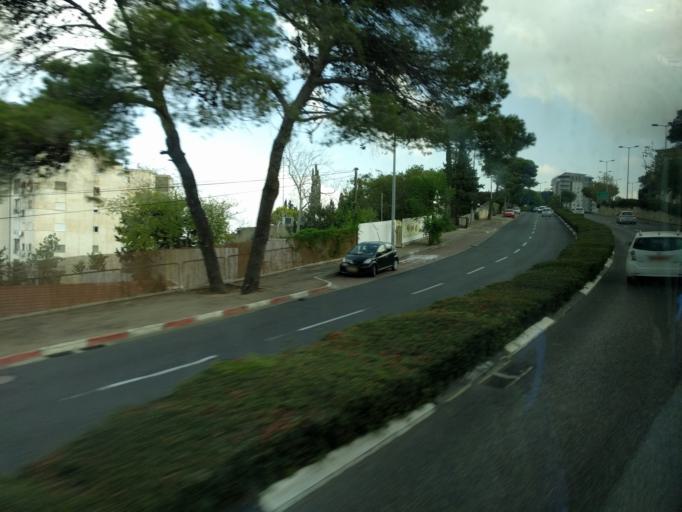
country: IL
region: Haifa
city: Nesher
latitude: 32.7684
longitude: 35.0082
